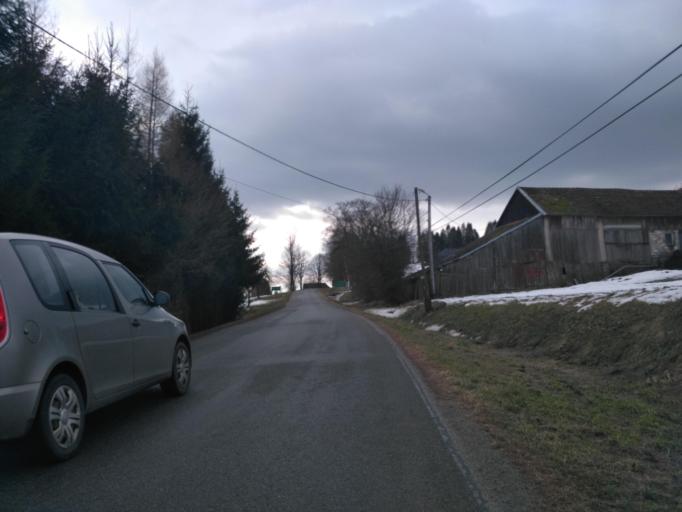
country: PL
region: Subcarpathian Voivodeship
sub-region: Powiat sanocki
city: Strachocina
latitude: 49.6161
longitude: 22.1494
